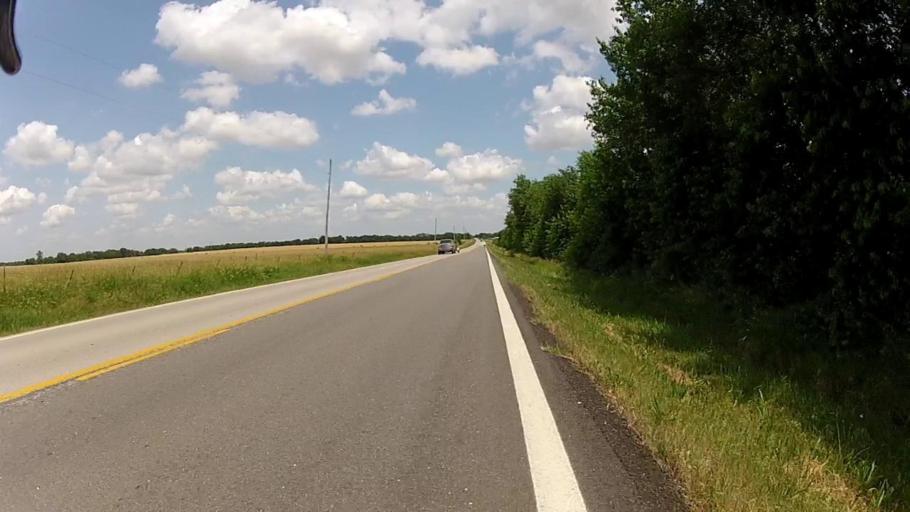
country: US
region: Kansas
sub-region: Labette County
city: Altamont
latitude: 37.1926
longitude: -95.3434
